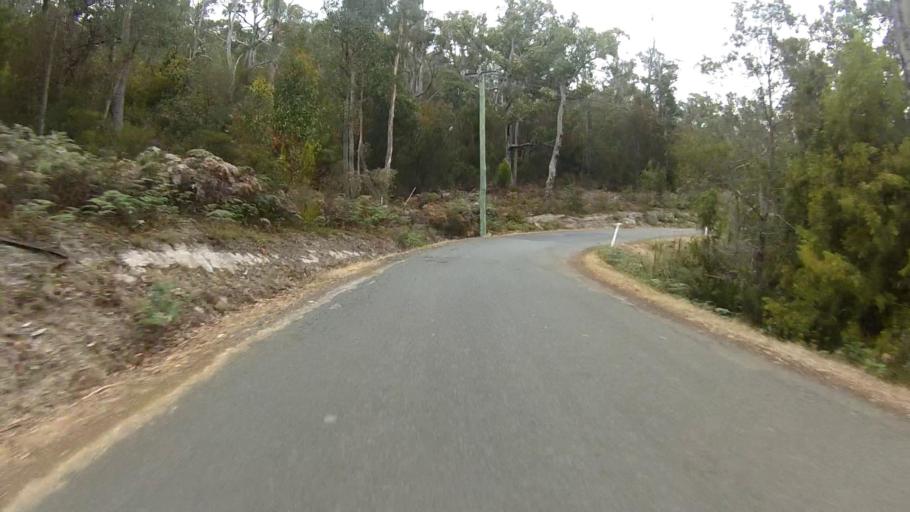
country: AU
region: Tasmania
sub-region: Huon Valley
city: Cygnet
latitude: -43.2170
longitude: 147.0973
